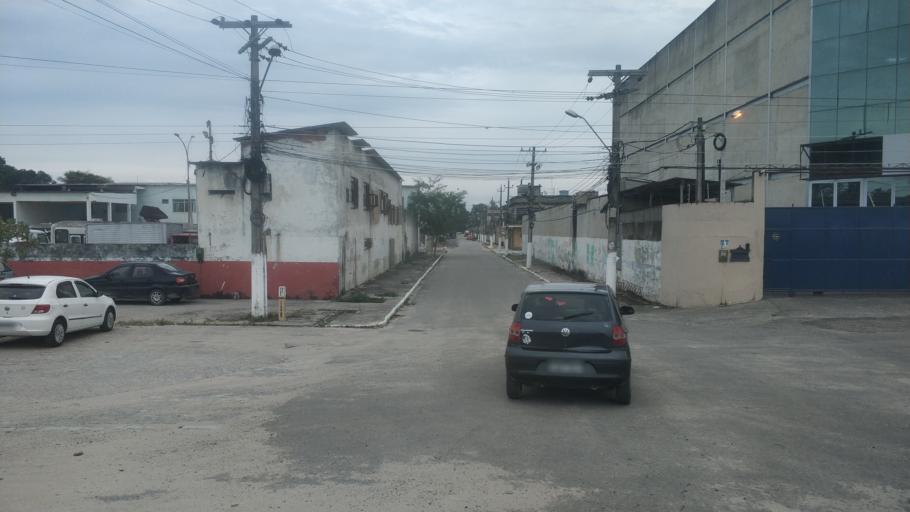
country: BR
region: Rio de Janeiro
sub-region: Seropedica
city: Seropedica
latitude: -22.7929
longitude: -43.6500
